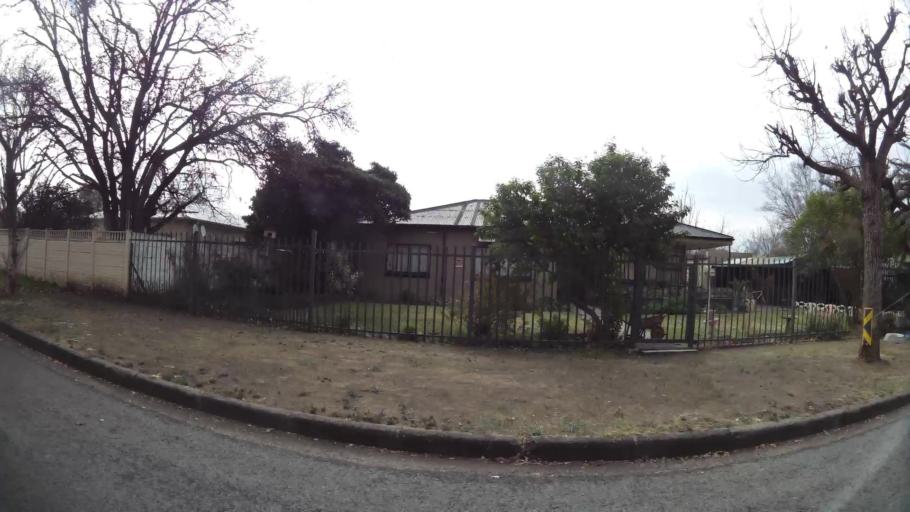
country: ZA
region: Orange Free State
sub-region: Mangaung Metropolitan Municipality
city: Bloemfontein
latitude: -29.0856
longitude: 26.2522
